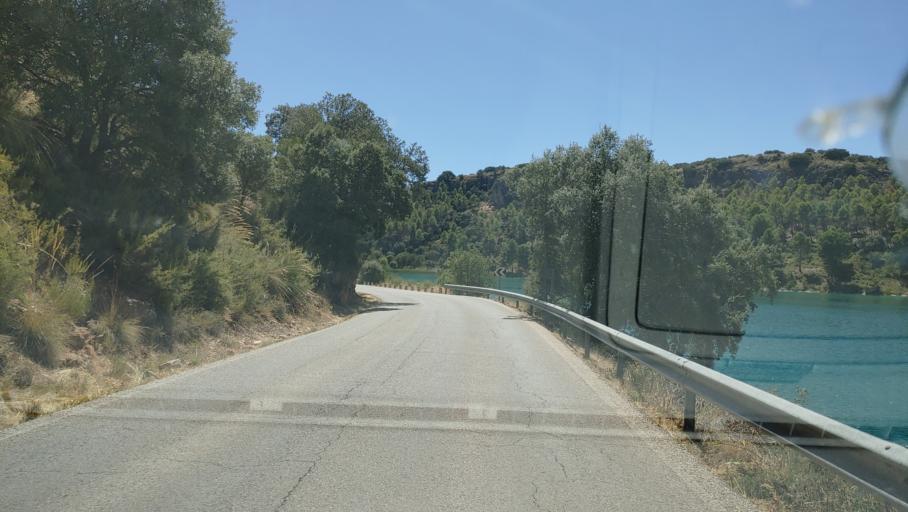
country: ES
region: Castille-La Mancha
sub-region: Provincia de Ciudad Real
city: Ruidera
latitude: 38.9427
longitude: -2.8541
